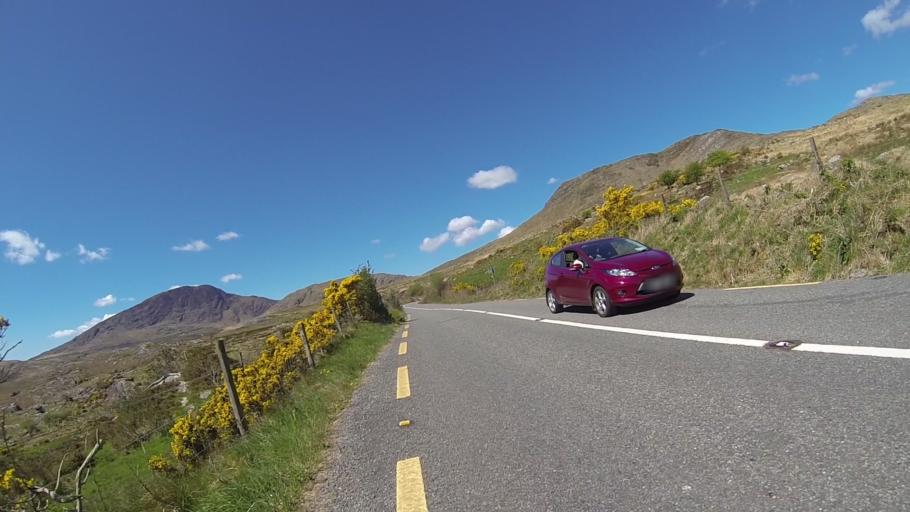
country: IE
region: Munster
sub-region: Ciarrai
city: Kenmare
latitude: 51.9254
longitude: -9.6344
